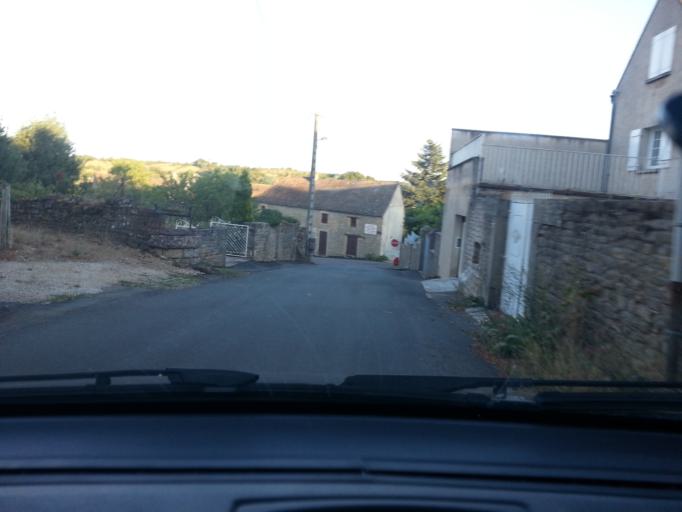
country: FR
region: Bourgogne
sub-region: Departement de Saone-et-Loire
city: Buxy
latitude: 46.7565
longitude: 4.6898
